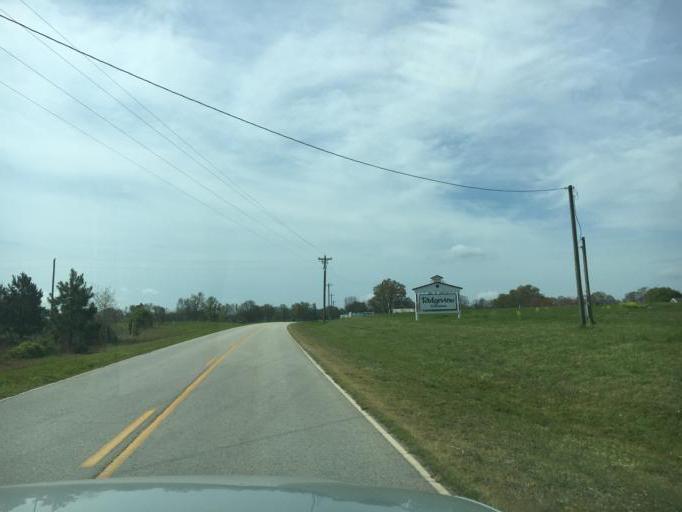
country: US
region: Georgia
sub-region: Franklin County
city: Lavonia
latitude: 34.4066
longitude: -83.0763
